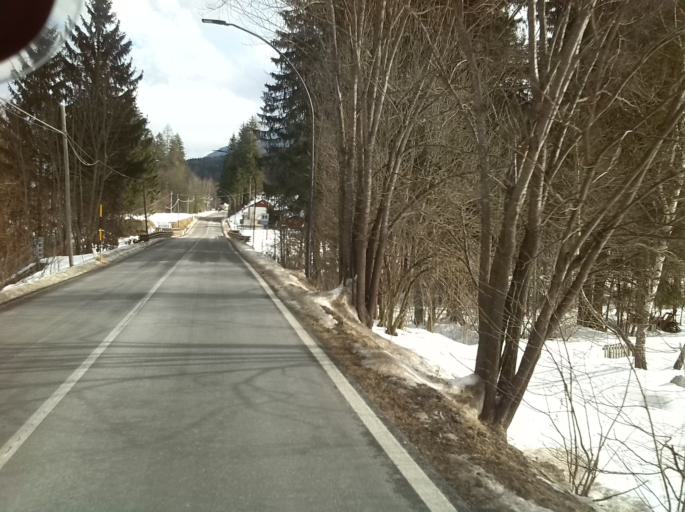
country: IT
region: Friuli Venezia Giulia
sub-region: Provincia di Udine
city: Tarvisio
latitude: 46.4966
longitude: 13.6351
